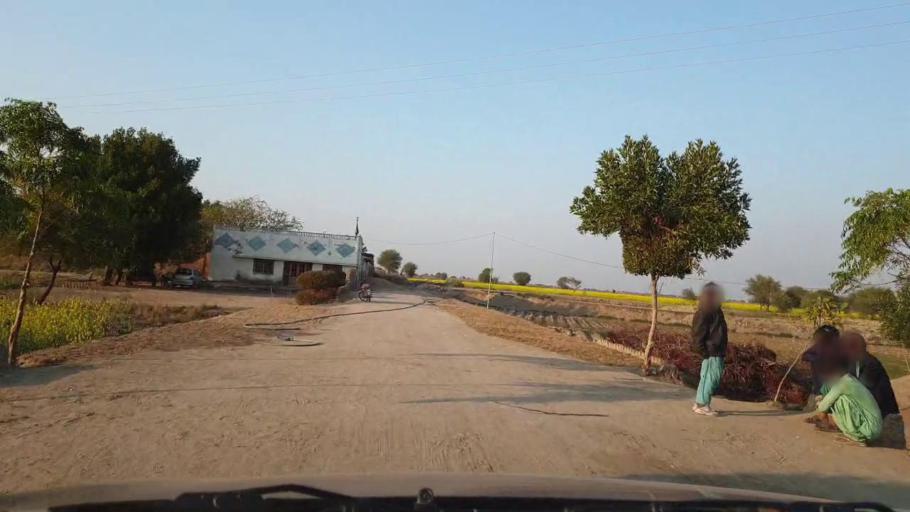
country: PK
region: Sindh
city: Jhol
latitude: 25.9340
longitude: 68.9333
